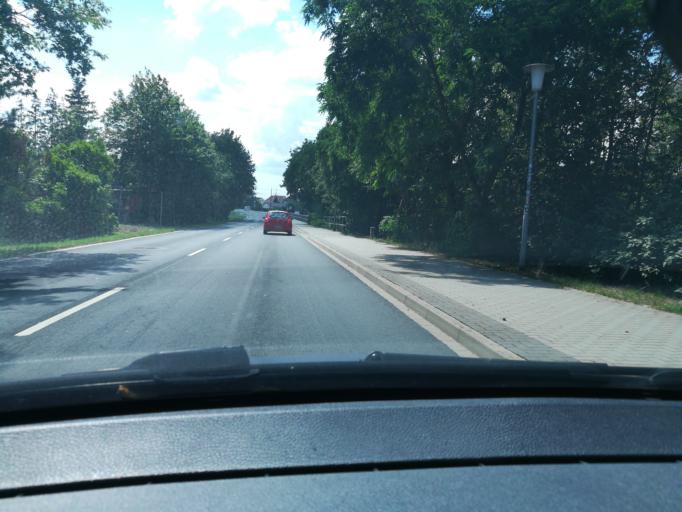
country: DE
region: Saxony-Anhalt
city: Zielitz
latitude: 52.2792
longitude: 11.6555
